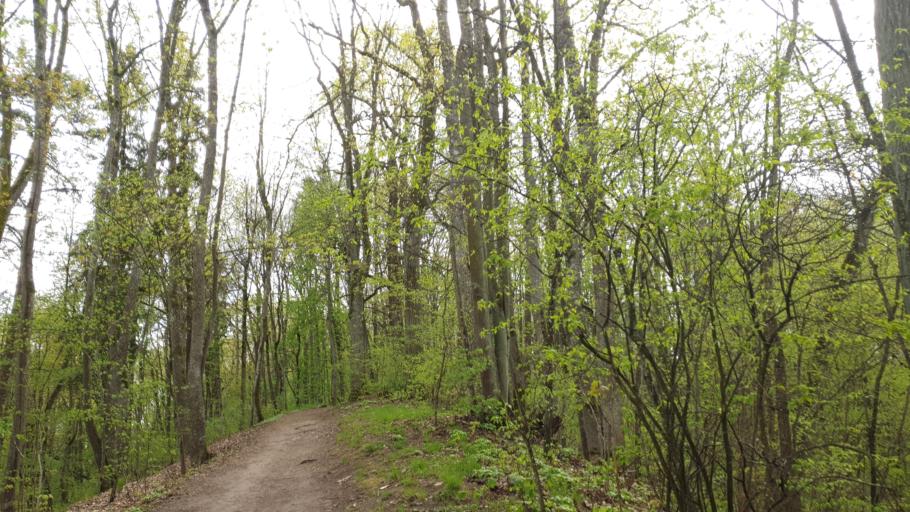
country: LT
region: Kauno apskritis
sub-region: Kauno rajonas
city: Akademija (Kaunas)
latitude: 54.9455
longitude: 23.7856
